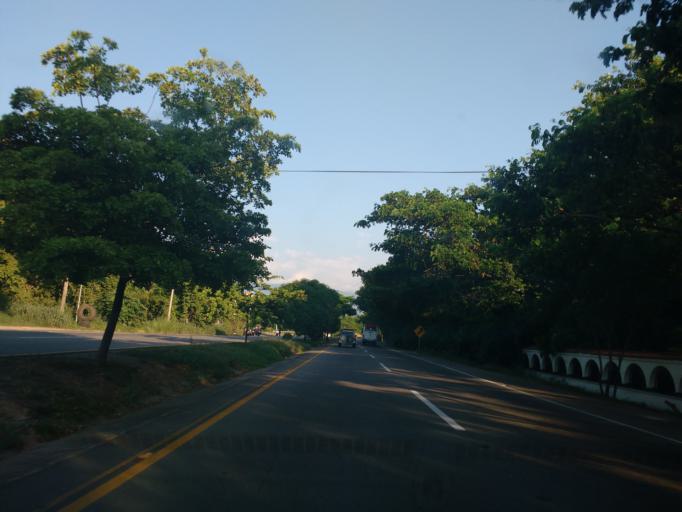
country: CO
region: Tolima
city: Melgar
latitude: 4.2220
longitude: -74.6941
